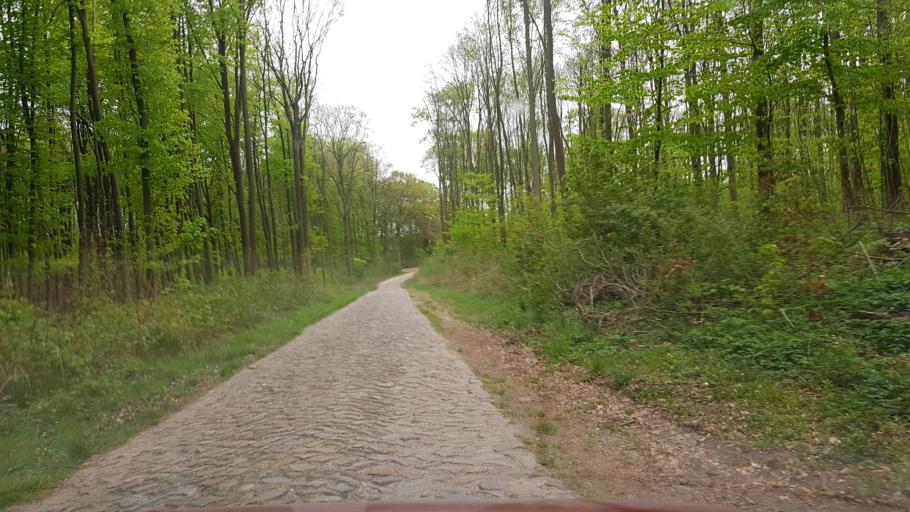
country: PL
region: West Pomeranian Voivodeship
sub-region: Powiat gryfinski
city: Stare Czarnowo
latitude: 53.2923
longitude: 14.7263
